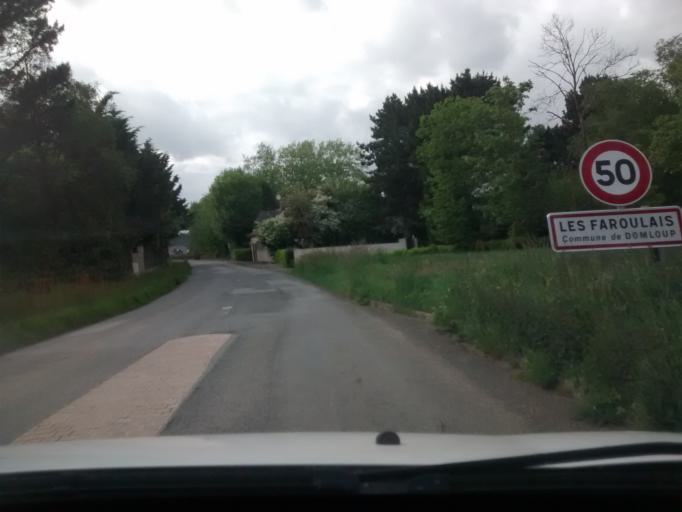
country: FR
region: Brittany
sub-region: Departement d'Ille-et-Vilaine
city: Noyal-sur-Vilaine
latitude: 48.0854
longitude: -1.5481
